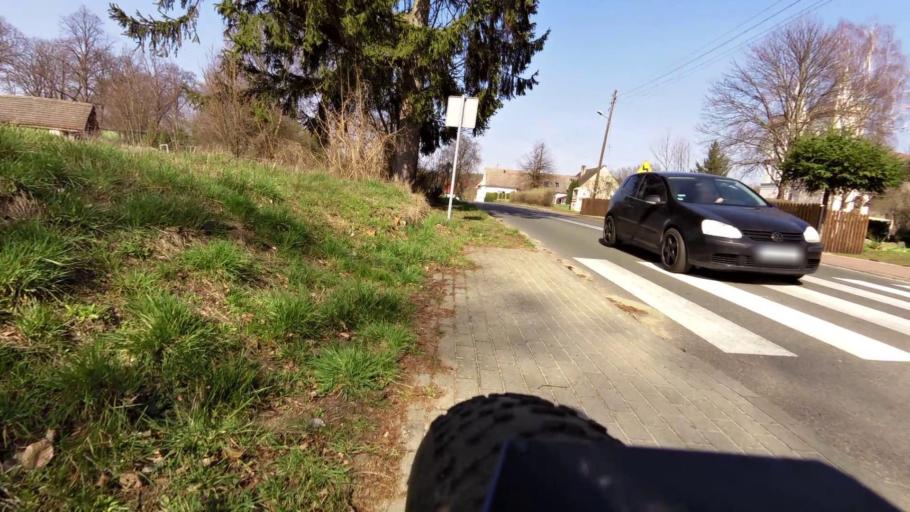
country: PL
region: Lubusz
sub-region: Powiat slubicki
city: Cybinka
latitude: 52.2216
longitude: 14.8445
